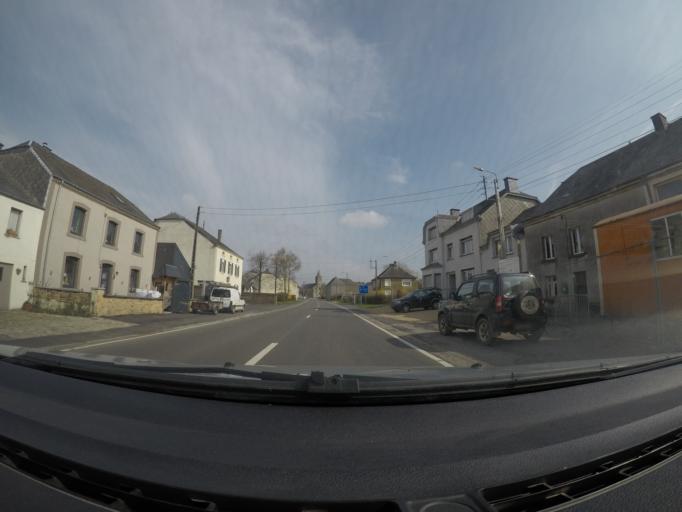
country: BE
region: Wallonia
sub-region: Province du Luxembourg
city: Chiny
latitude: 49.7025
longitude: 5.4230
